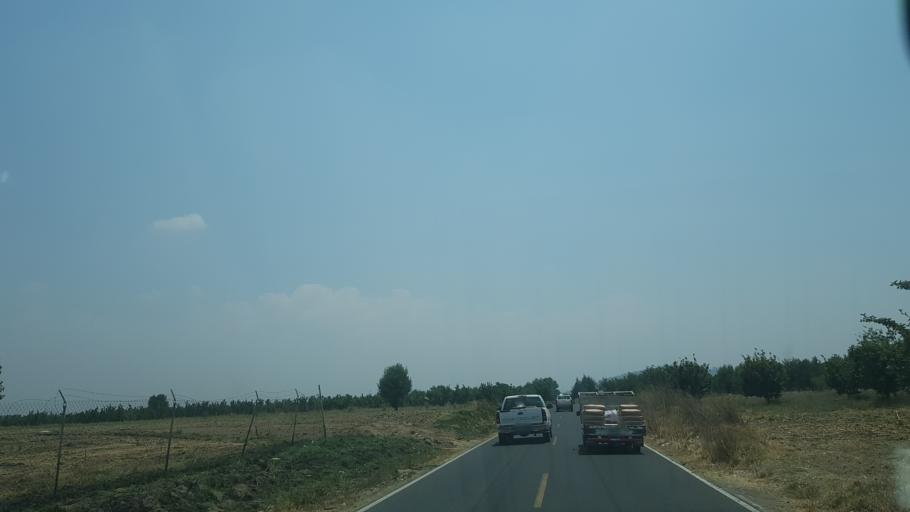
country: MX
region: Puebla
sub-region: San Jeronimo Tecuanipan
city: San Miguel Papaxtla
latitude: 19.0939
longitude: -98.4000
